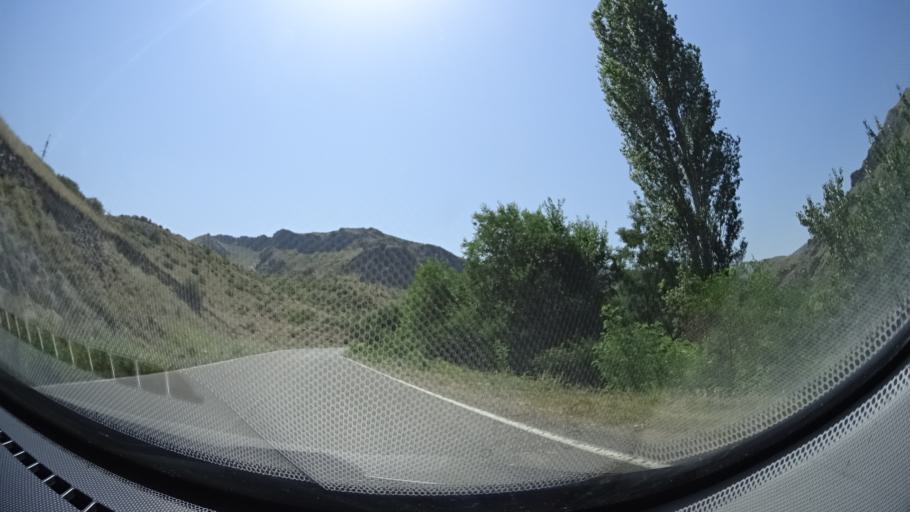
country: GE
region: Samtskhe-Javakheti
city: Aspindza
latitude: 41.4966
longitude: 43.2647
